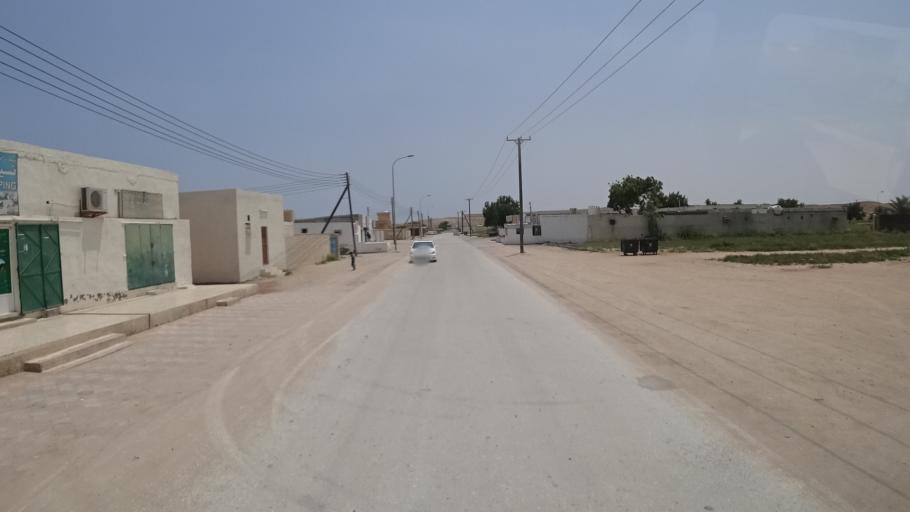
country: OM
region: Ash Sharqiyah
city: Sur
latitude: 22.5113
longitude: 59.7982
